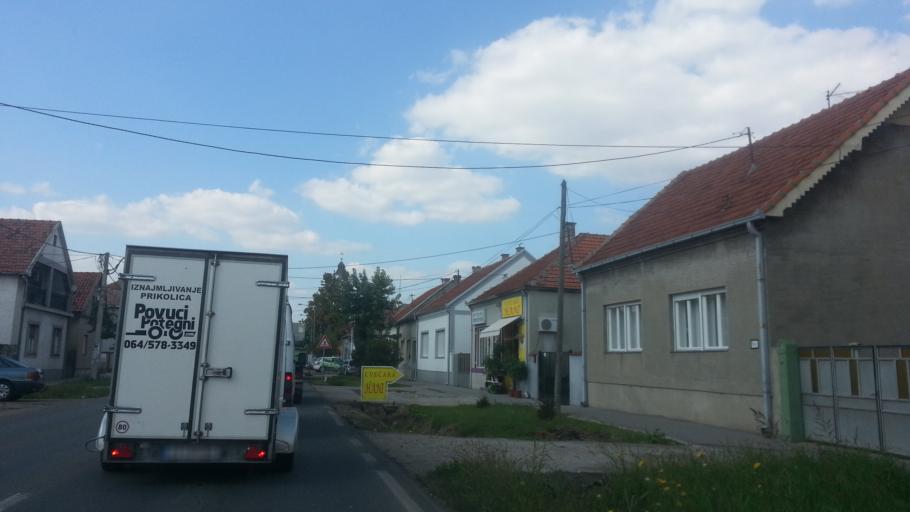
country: RS
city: Novi Banovci
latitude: 44.9051
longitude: 20.2767
